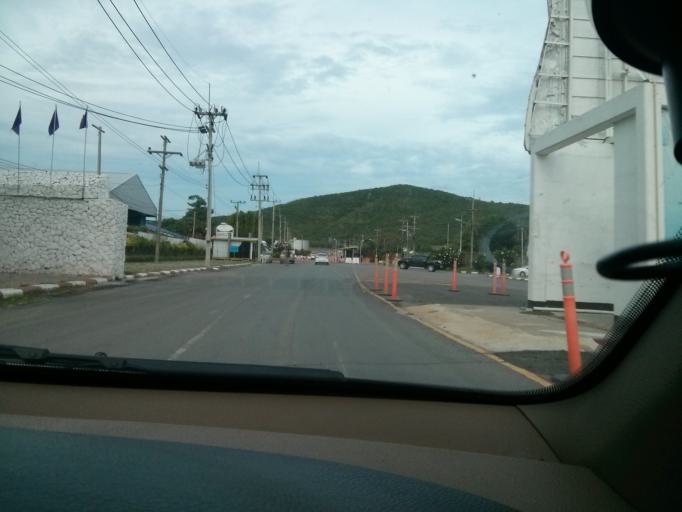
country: TH
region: Chon Buri
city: Sattahip
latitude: 12.6236
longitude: 100.9279
